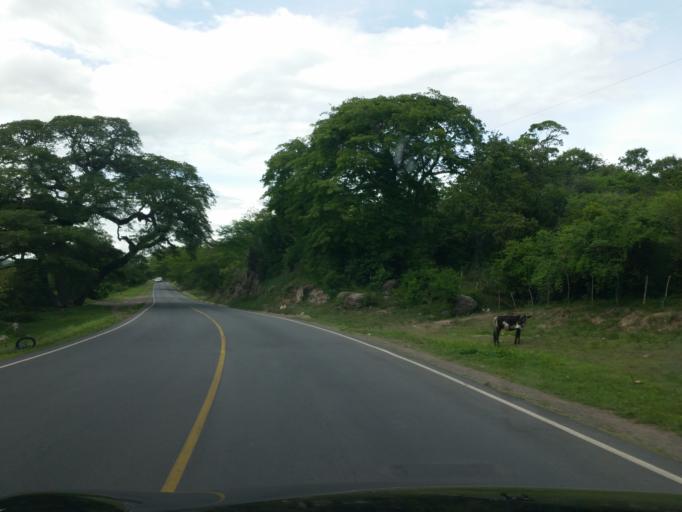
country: NI
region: Matagalpa
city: Terrabona
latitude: 12.5760
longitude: -86.0419
